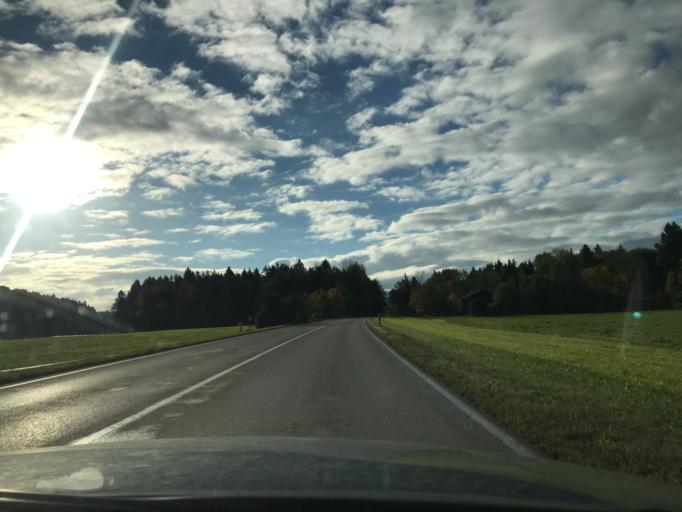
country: DE
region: Bavaria
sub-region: Upper Bavaria
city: Dietramszell
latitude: 47.8200
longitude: 11.5438
